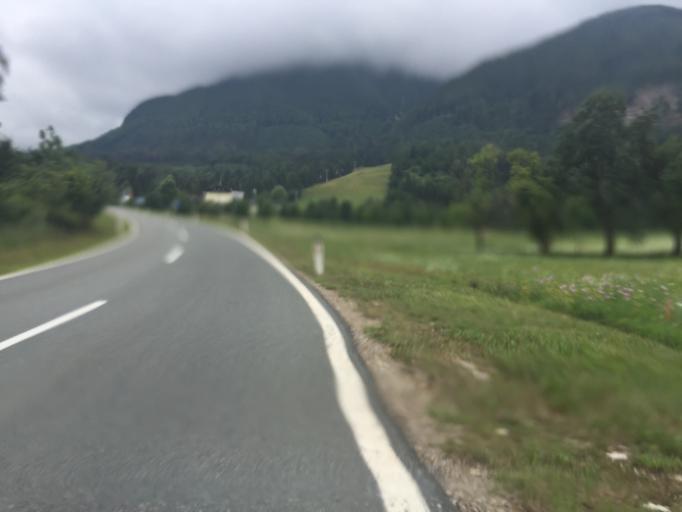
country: AT
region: Carinthia
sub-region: Politischer Bezirk Volkermarkt
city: Feistritz ob Bleiburg
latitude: 46.5446
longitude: 14.7725
